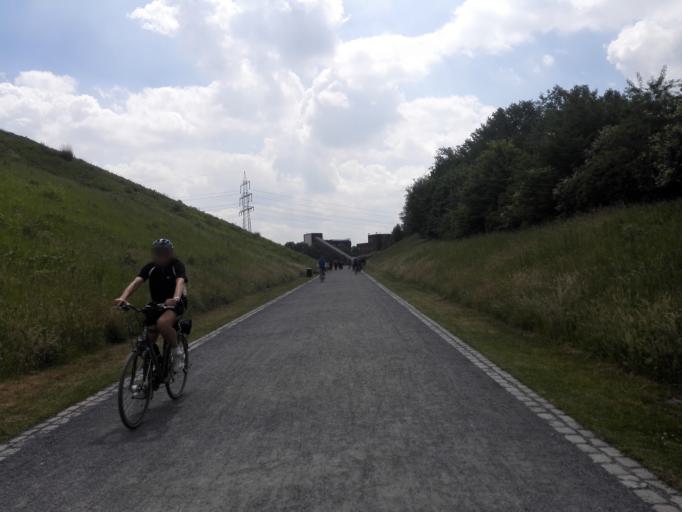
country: DE
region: North Rhine-Westphalia
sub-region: Regierungsbezirk Munster
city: Gladbeck
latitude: 51.5263
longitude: 7.0307
